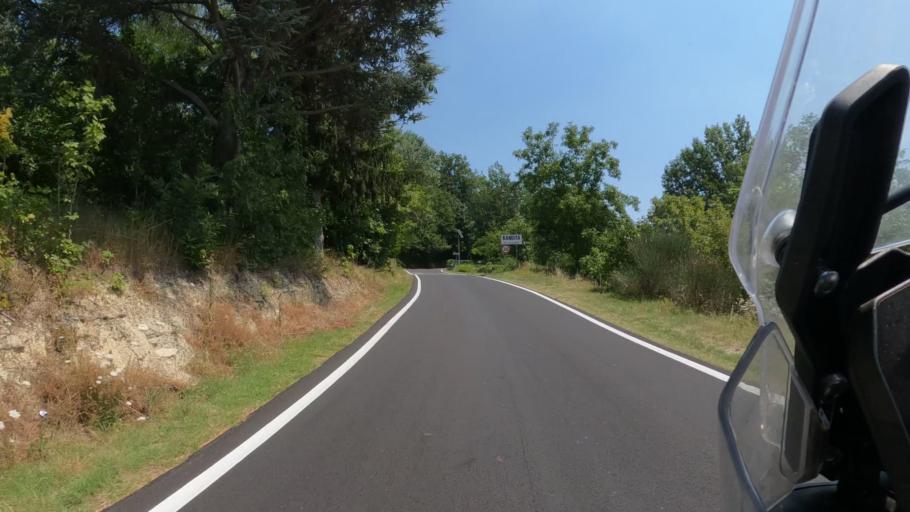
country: IT
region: Piedmont
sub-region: Provincia di Alessandria
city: Cassinelle-Concentrico
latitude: 44.5787
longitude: 8.5482
